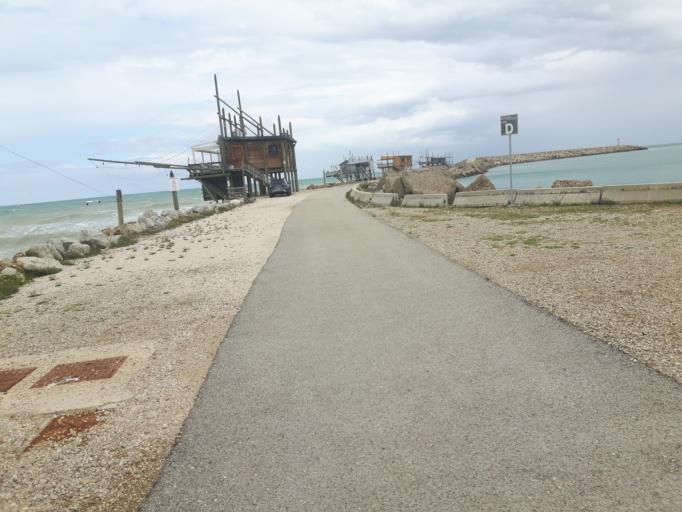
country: IT
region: Abruzzo
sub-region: Provincia di Chieti
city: Vasto
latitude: 42.1752
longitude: 14.7082
